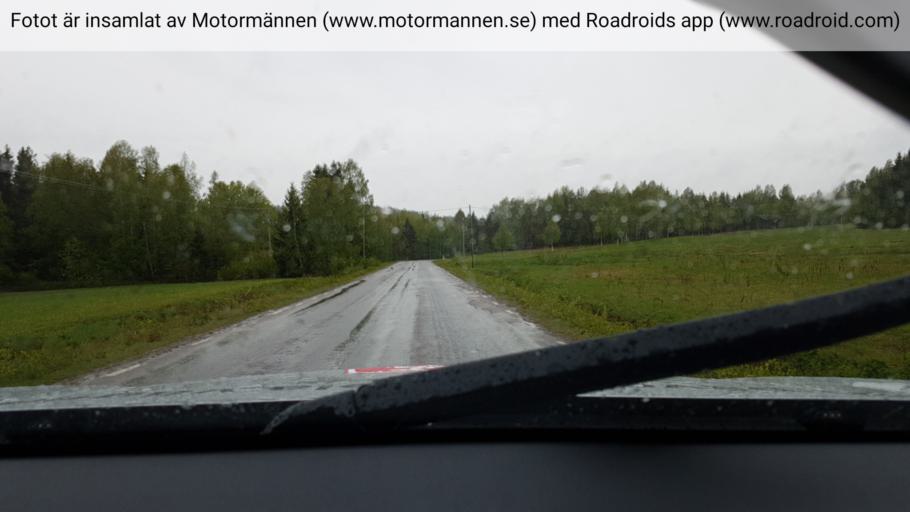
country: SE
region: Vaesterbotten
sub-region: Vannas Kommun
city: Vaennaes
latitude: 63.8697
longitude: 19.6735
